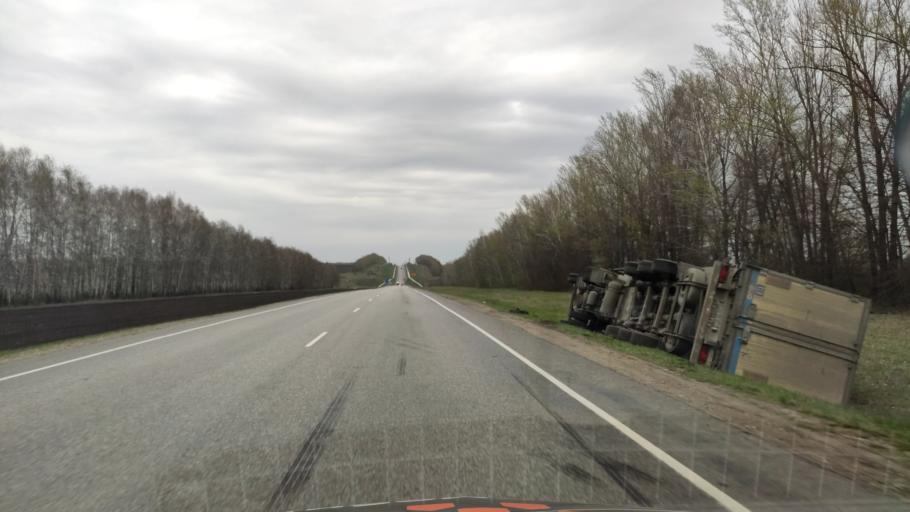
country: RU
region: Kursk
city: Olym
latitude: 51.5547
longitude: 38.2263
